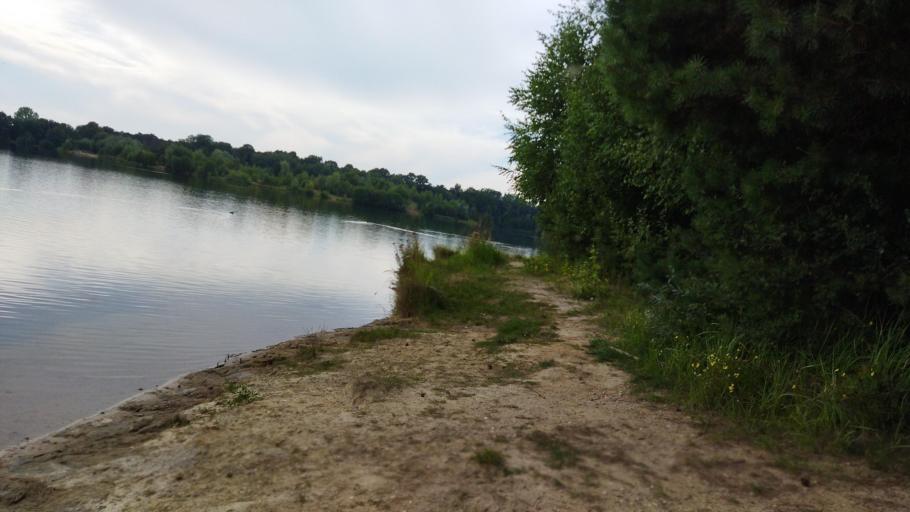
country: DE
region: Lower Saxony
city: Glandorf
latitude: 52.0982
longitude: 8.0442
